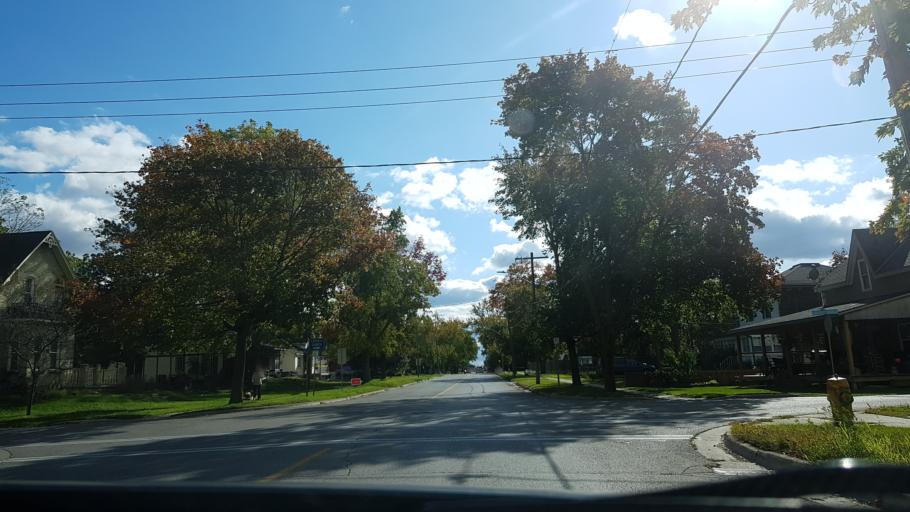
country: CA
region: Ontario
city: South Huron
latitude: 43.1582
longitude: -81.6854
